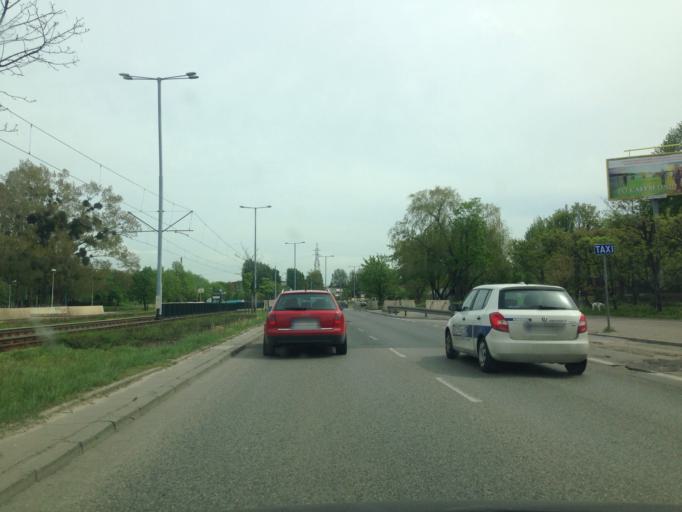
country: PL
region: Pomeranian Voivodeship
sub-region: Gdansk
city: Gdansk
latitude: 54.3927
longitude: 18.6046
